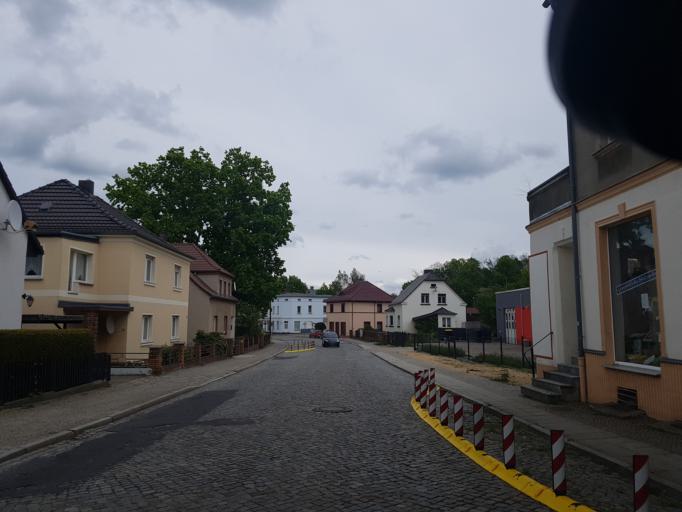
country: DE
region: Brandenburg
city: Tschernitz
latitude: 51.6139
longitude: 14.5952
